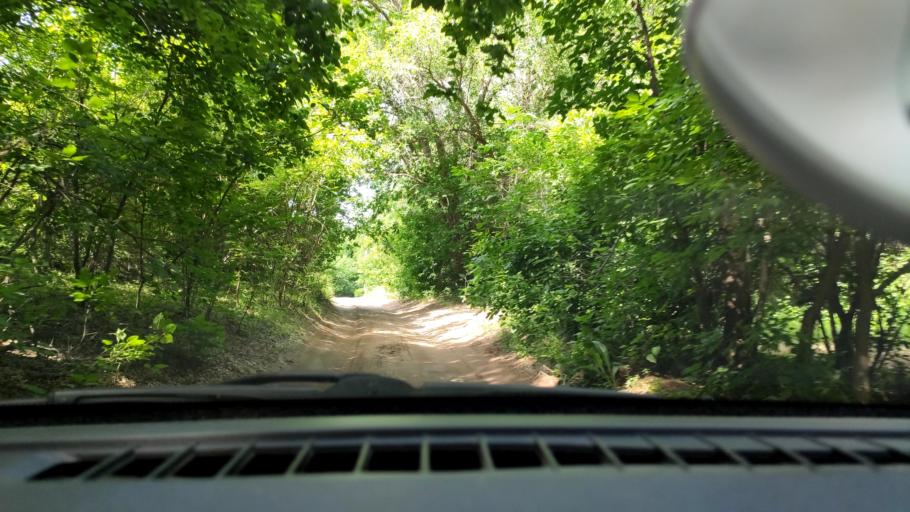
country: RU
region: Samara
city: Samara
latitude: 53.1278
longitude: 50.1800
